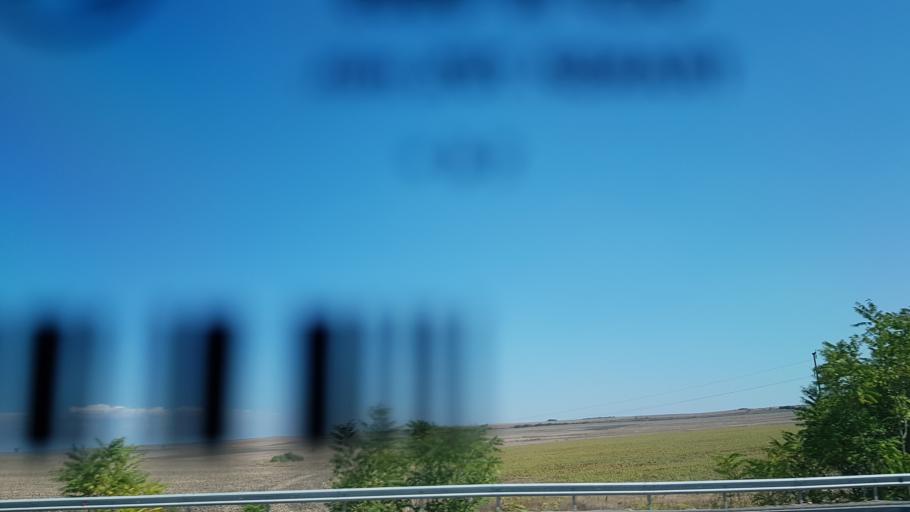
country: TR
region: Kirklareli
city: Luleburgaz
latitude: 41.4231
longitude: 27.3844
